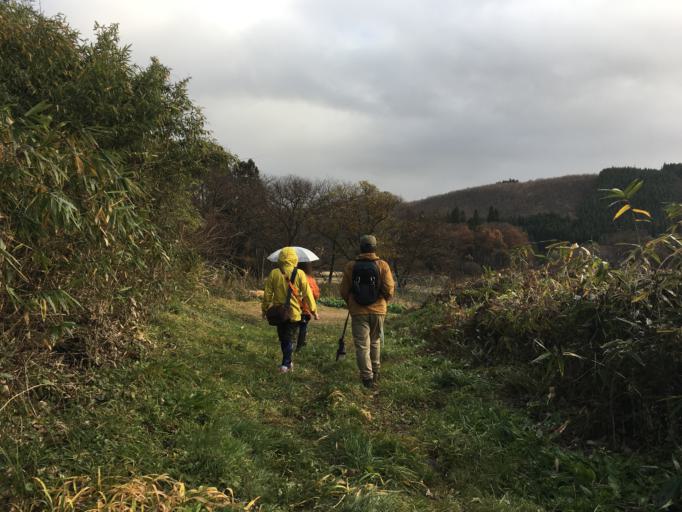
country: JP
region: Iwate
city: Ichinoseki
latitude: 38.9737
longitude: 140.9727
